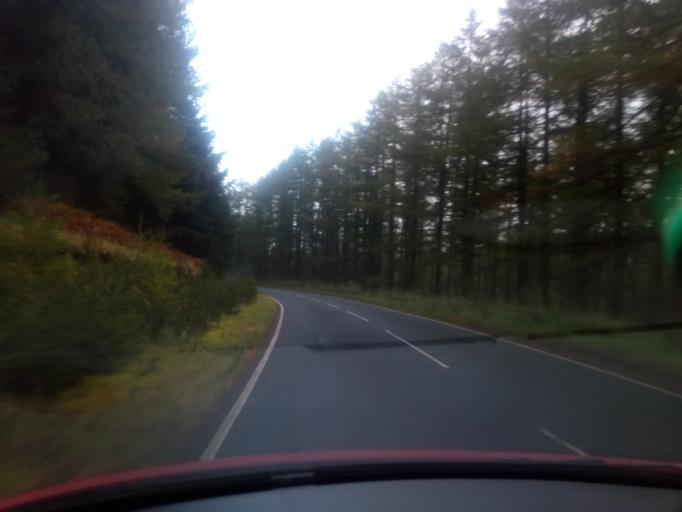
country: GB
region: Scotland
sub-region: The Scottish Borders
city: Hawick
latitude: 55.3336
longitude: -2.6483
